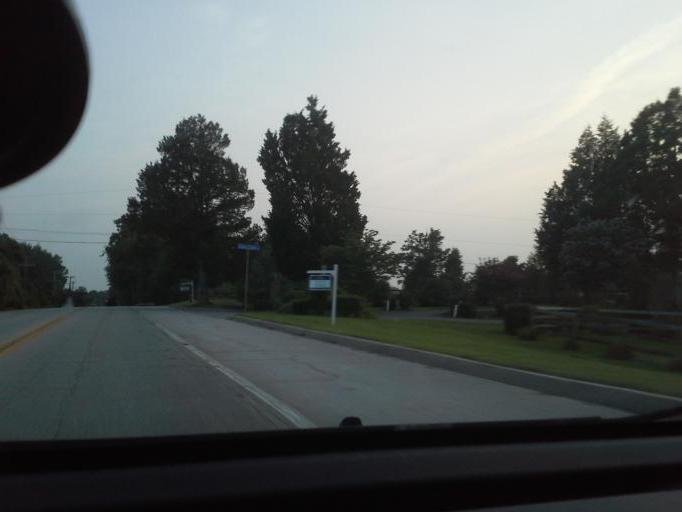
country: US
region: Maryland
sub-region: Anne Arundel County
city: Davidsonville
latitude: 38.8954
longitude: -76.5938
